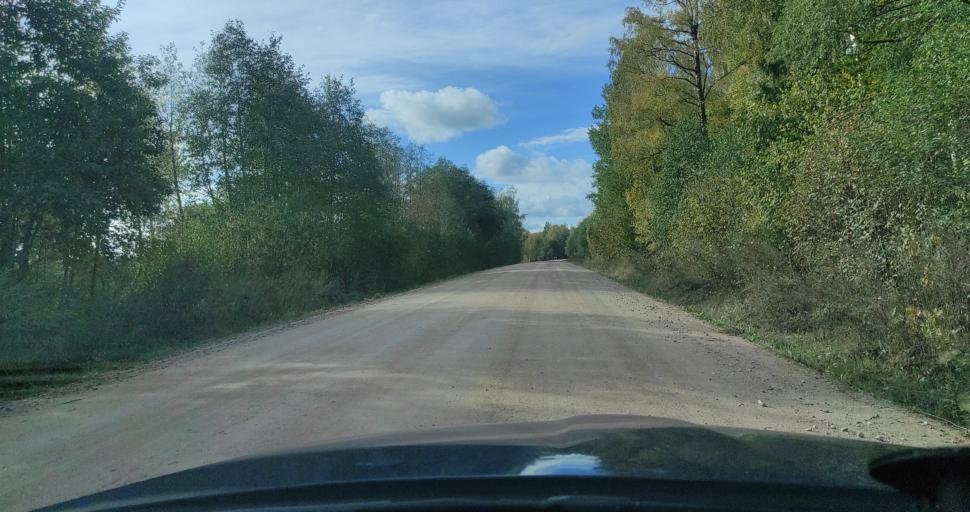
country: LV
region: Jaunpils
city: Jaunpils
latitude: 56.8296
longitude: 22.9763
